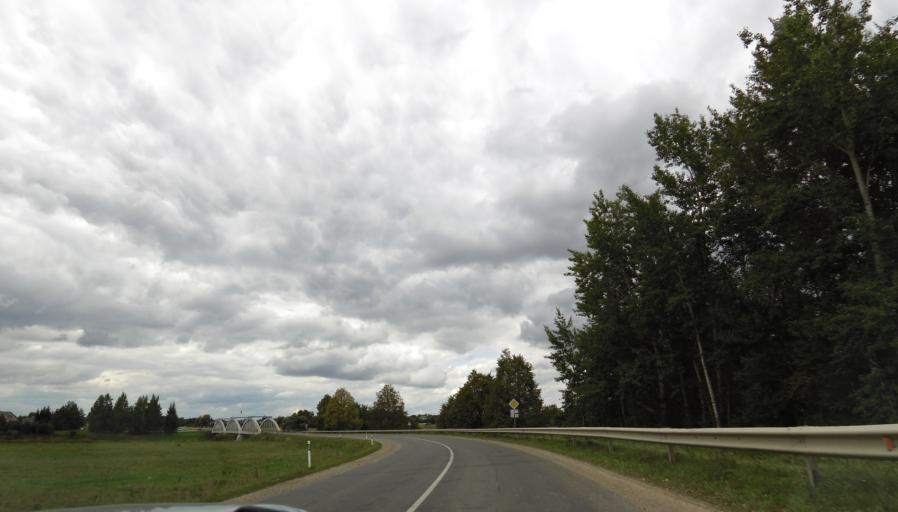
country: LT
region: Panevezys
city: Pasvalys
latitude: 56.0781
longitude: 24.3780
